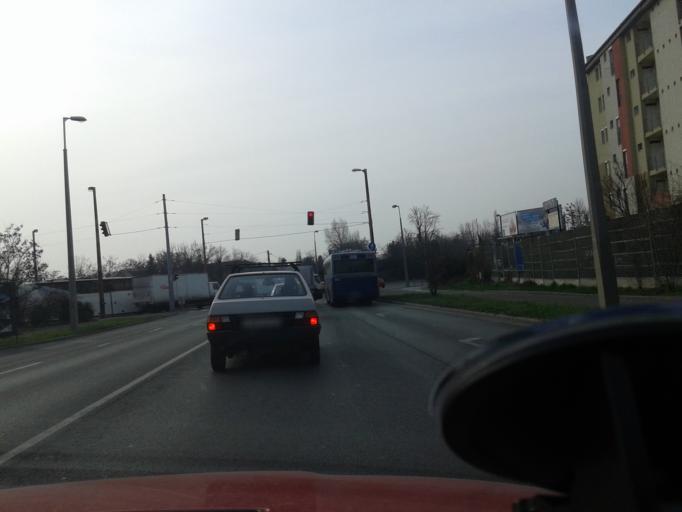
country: HU
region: Budapest
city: Budapest XI. keruelet
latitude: 47.4562
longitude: 19.0237
